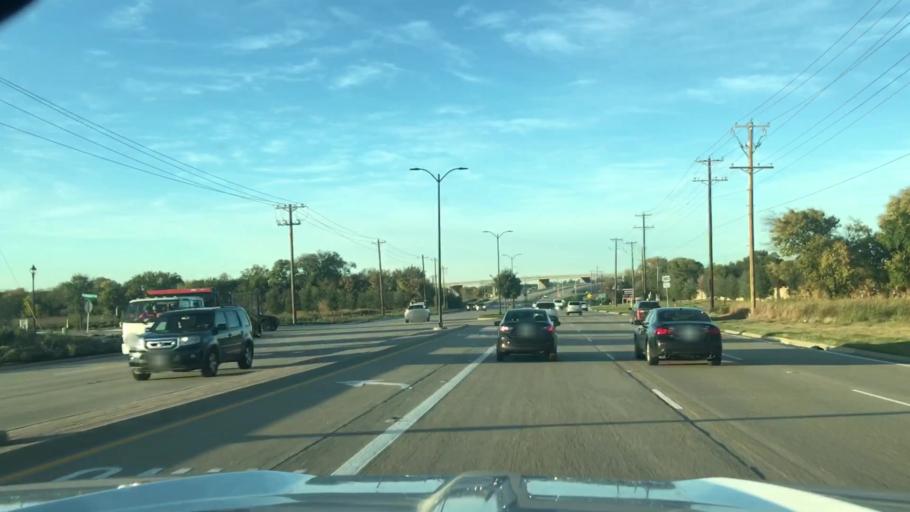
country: US
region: Texas
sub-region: Collin County
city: Prosper
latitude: 33.2110
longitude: -96.8026
